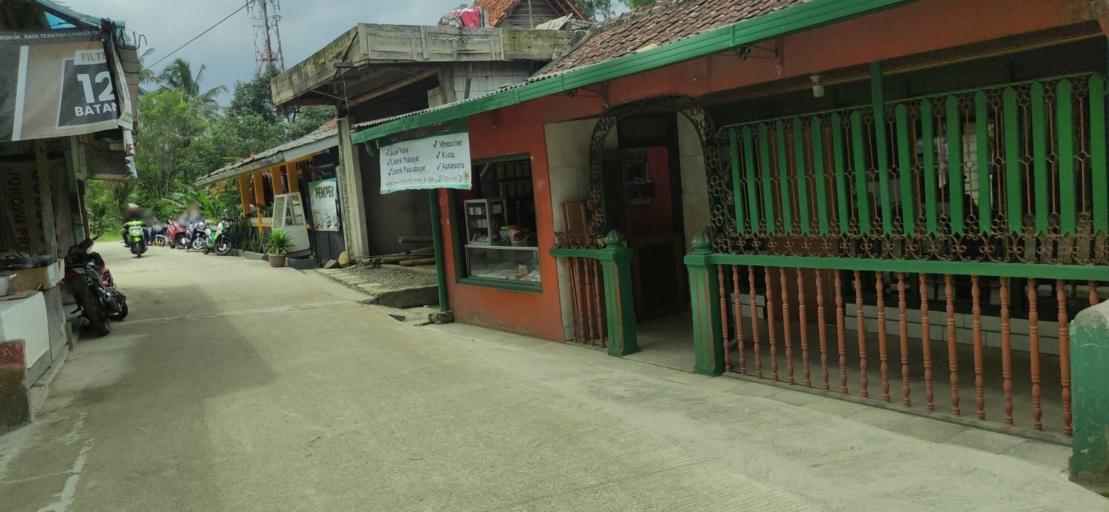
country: ID
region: West Java
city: Caringin
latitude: -6.6457
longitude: 106.9012
